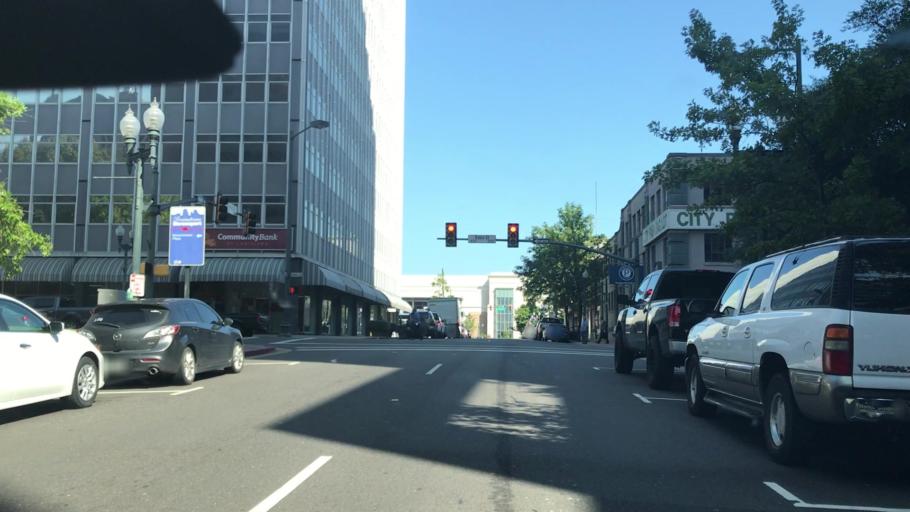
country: US
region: Louisiana
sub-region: Caddo Parish
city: Shreveport
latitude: 32.5142
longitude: -93.7493
